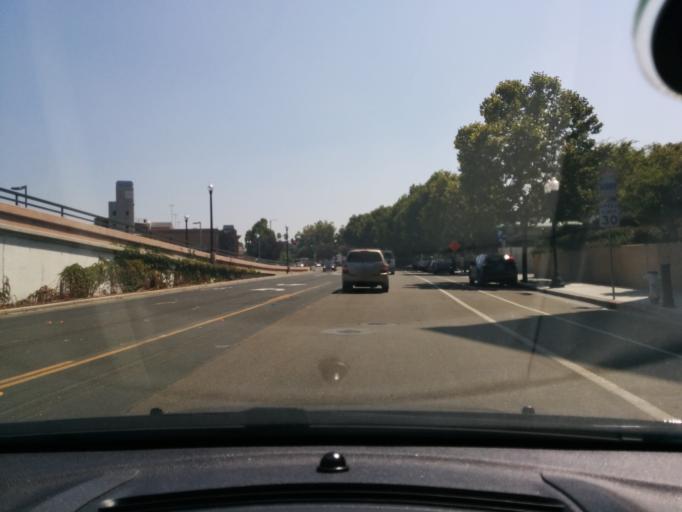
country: US
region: California
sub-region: Santa Clara County
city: Sunnyvale
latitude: 37.3788
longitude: -122.0326
